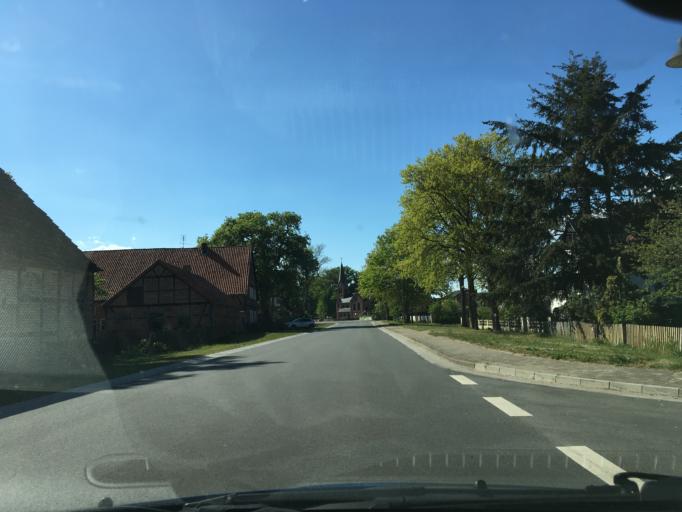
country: DE
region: Lower Saxony
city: Gartow
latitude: 53.0187
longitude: 11.5323
